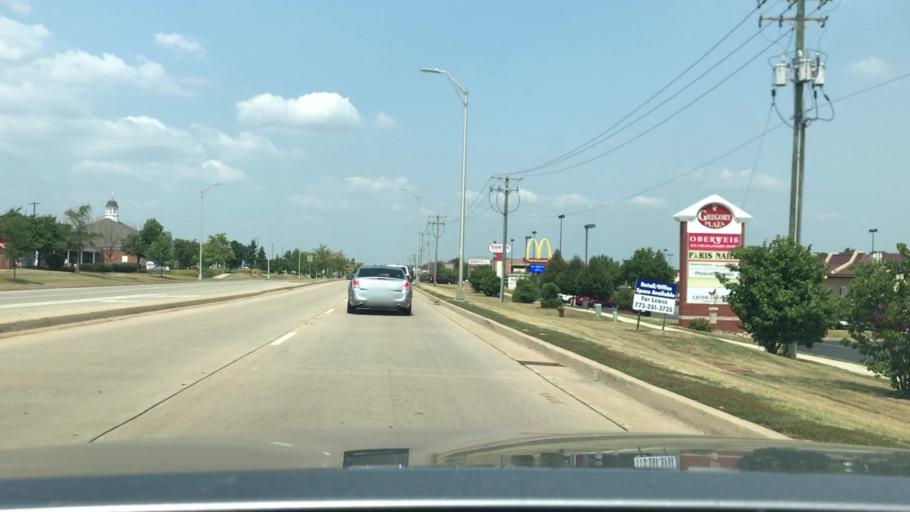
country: US
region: Illinois
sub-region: Will County
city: Shorewood
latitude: 41.5613
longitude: -88.2001
